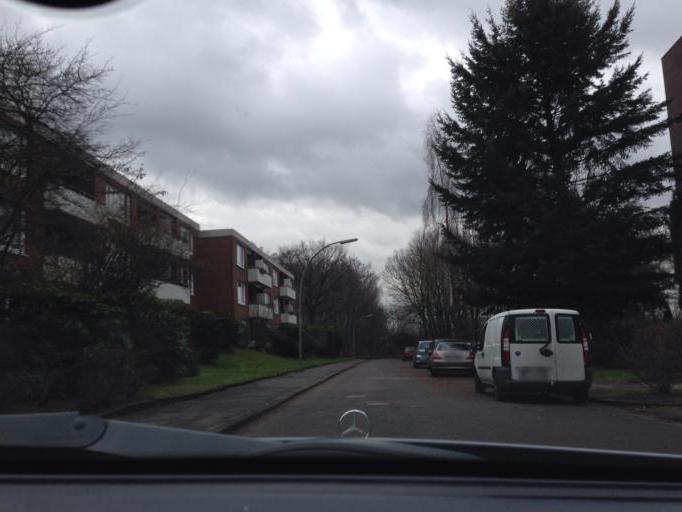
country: DE
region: Schleswig-Holstein
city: Barsbuettel
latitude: 53.5869
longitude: 10.1725
